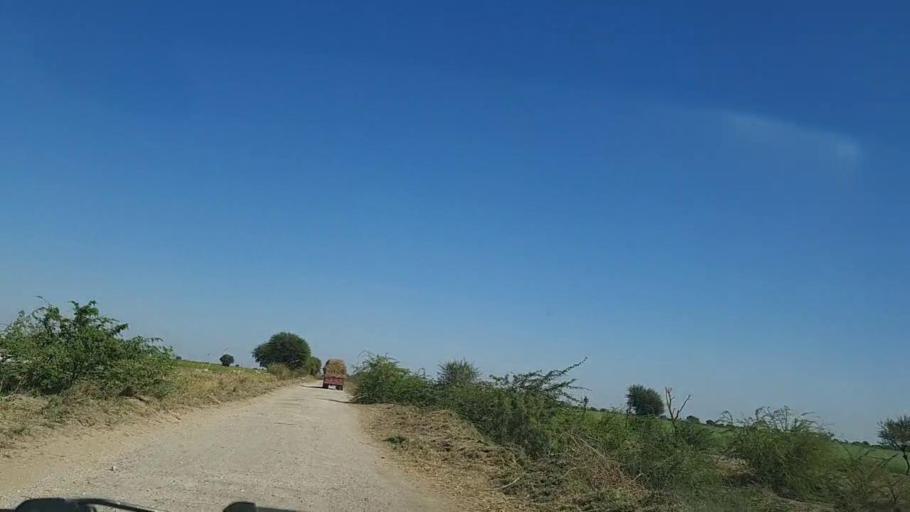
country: PK
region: Sindh
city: Pithoro
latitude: 25.5618
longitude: 69.4607
